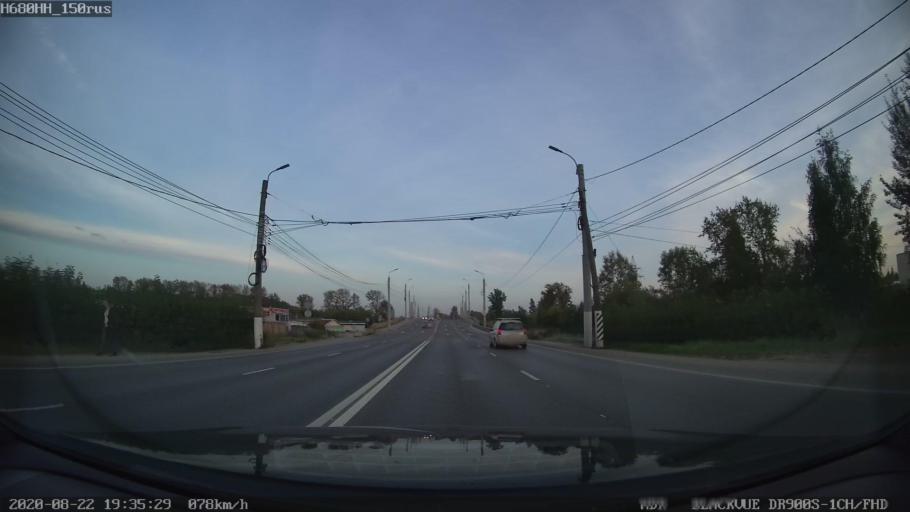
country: RU
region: Tverskaya
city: Tver
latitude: 56.8349
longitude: 35.9631
